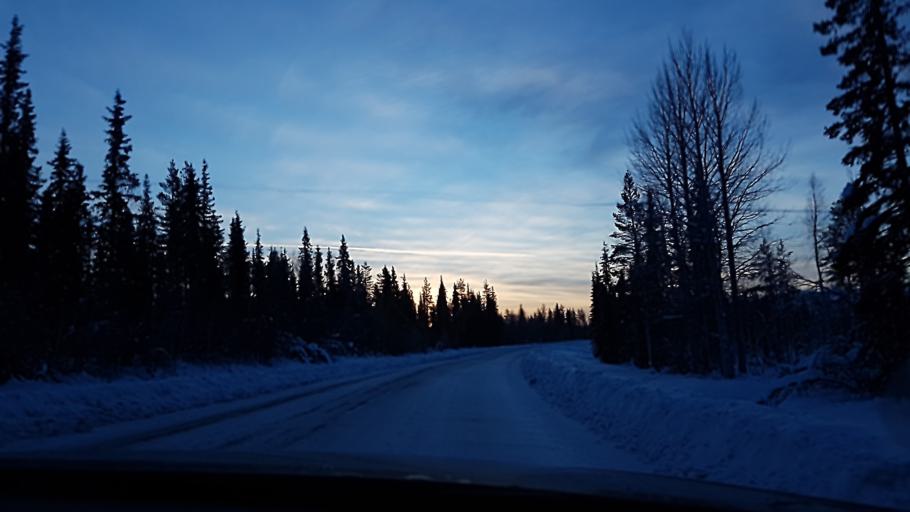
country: SE
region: Norrbotten
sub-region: Jokkmokks Kommun
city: Jokkmokk
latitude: 66.0981
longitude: 20.0700
